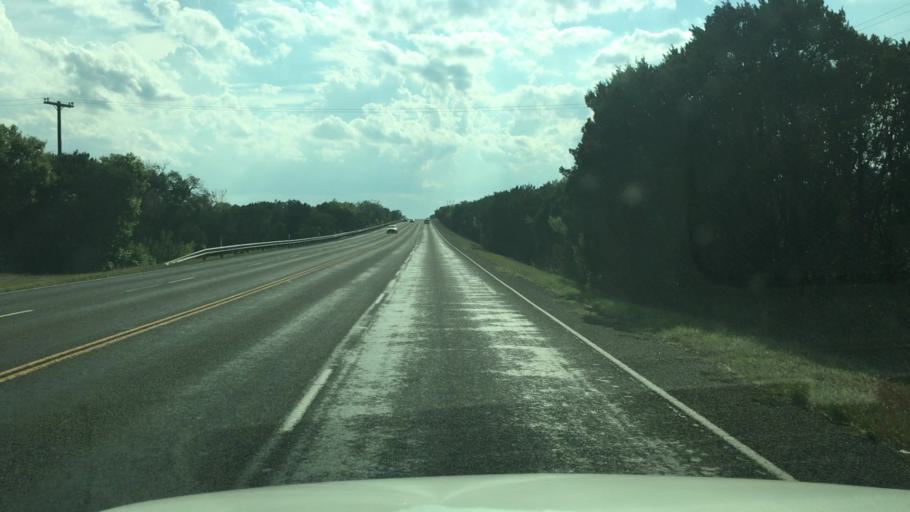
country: US
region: Texas
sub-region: Blanco County
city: Johnson City
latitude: 30.2099
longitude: -98.2907
